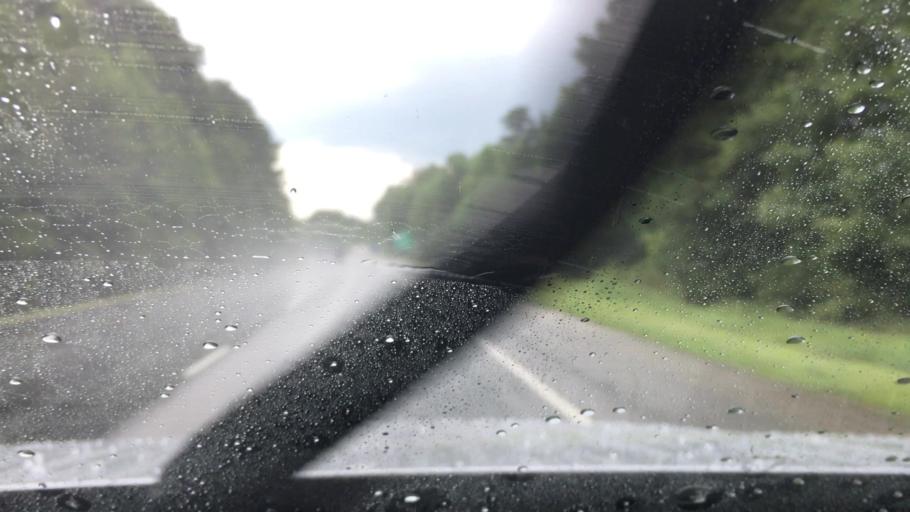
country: US
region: North Carolina
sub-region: Northampton County
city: Gaston
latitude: 36.4814
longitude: -77.6057
